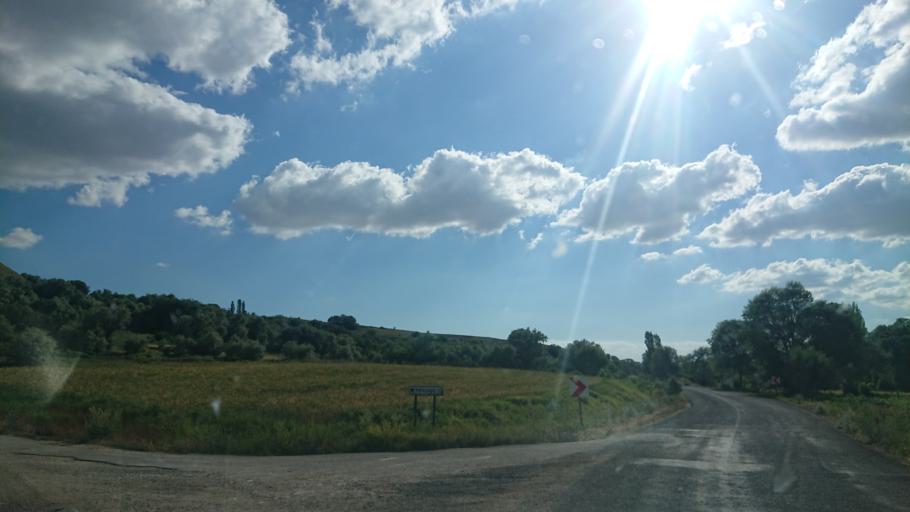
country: TR
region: Aksaray
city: Agacoren
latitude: 38.7571
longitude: 33.8875
